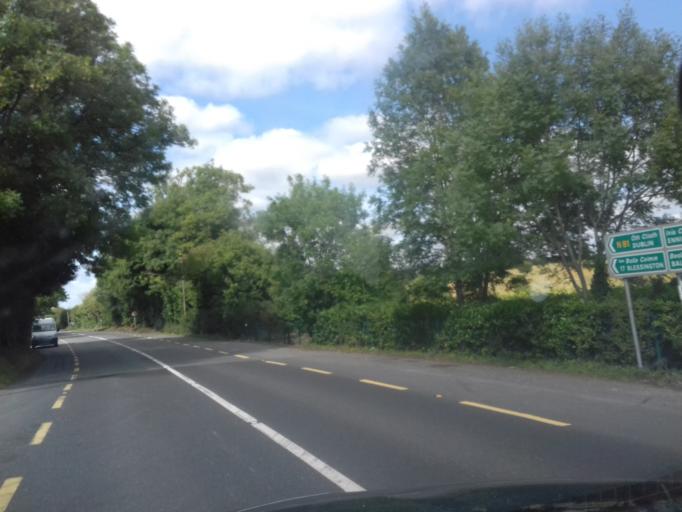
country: IE
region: Leinster
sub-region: Wicklow
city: Valleymount
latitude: 53.0374
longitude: -6.6354
